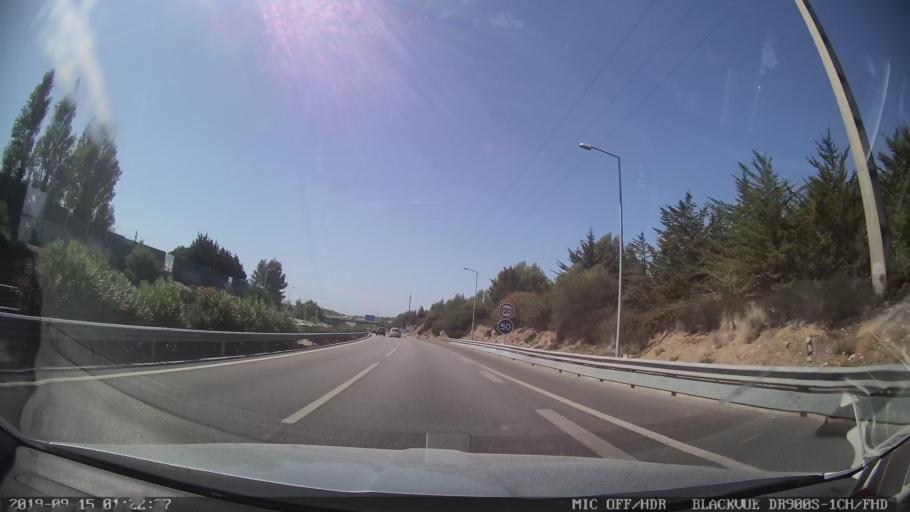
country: PT
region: Lisbon
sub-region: Cascais
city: Alcabideche
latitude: 38.7270
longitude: -9.4219
